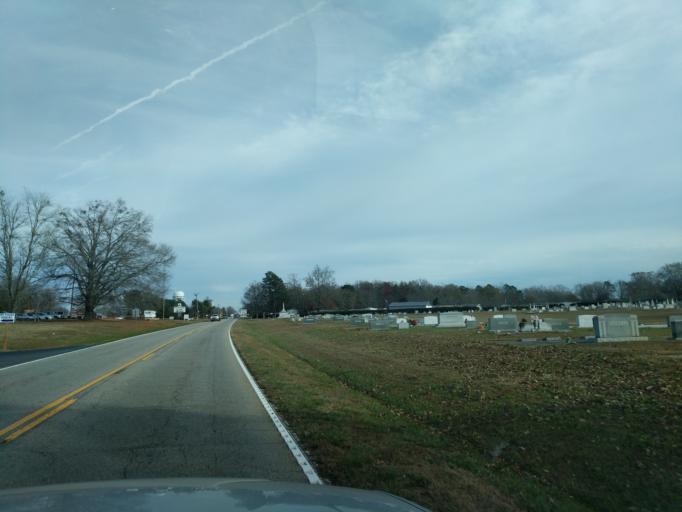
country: US
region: South Carolina
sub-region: Pickens County
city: Easley
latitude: 34.7181
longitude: -82.5811
